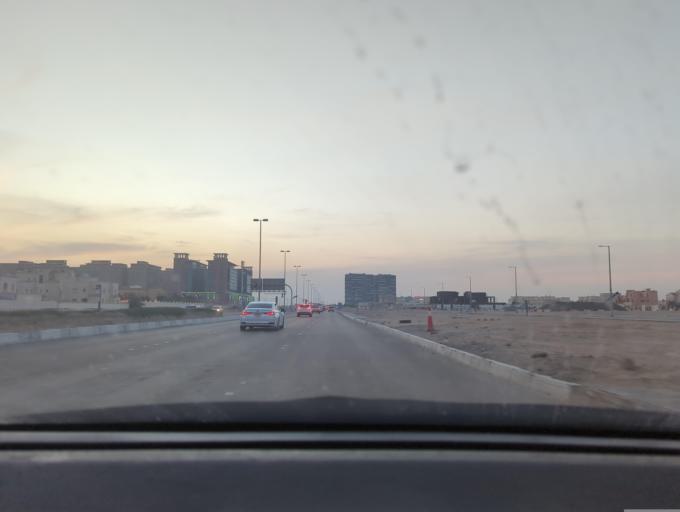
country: AE
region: Abu Dhabi
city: Abu Dhabi
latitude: 24.3747
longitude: 54.5447
